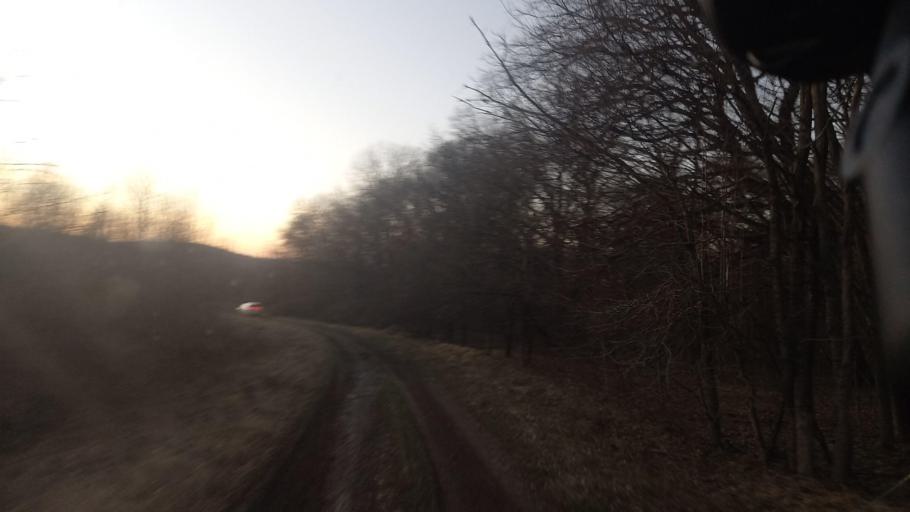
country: RU
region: Krasnodarskiy
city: Smolenskaya
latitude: 44.7268
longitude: 38.8405
